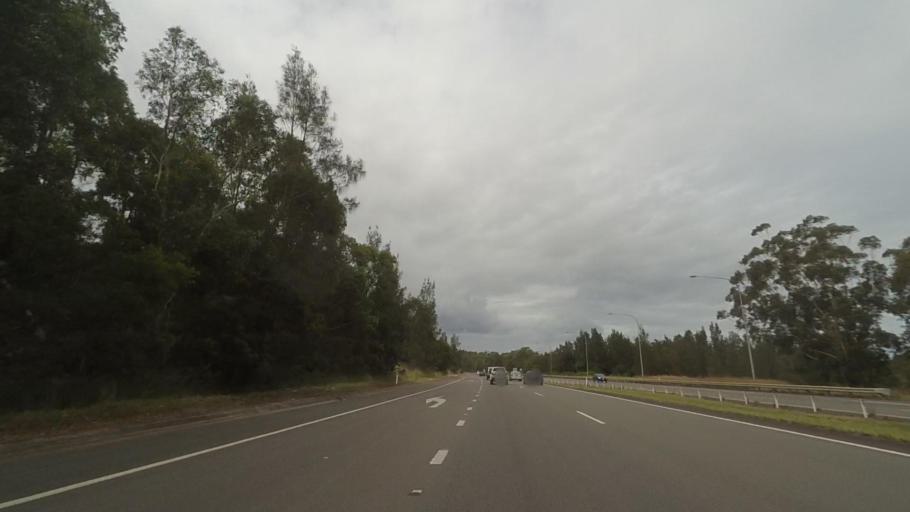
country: AU
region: New South Wales
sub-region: Port Stephens Shire
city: Raymond Terrace
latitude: -32.7429
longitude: 151.7749
